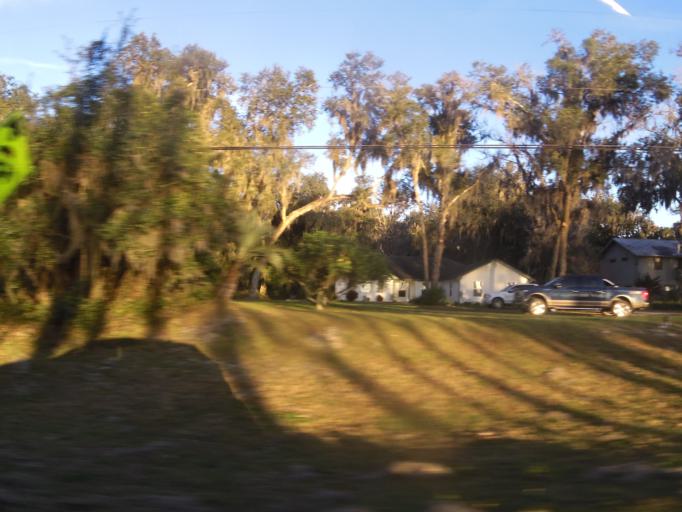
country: US
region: Florida
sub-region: Clay County
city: Green Cove Springs
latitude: 29.8503
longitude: -81.5570
